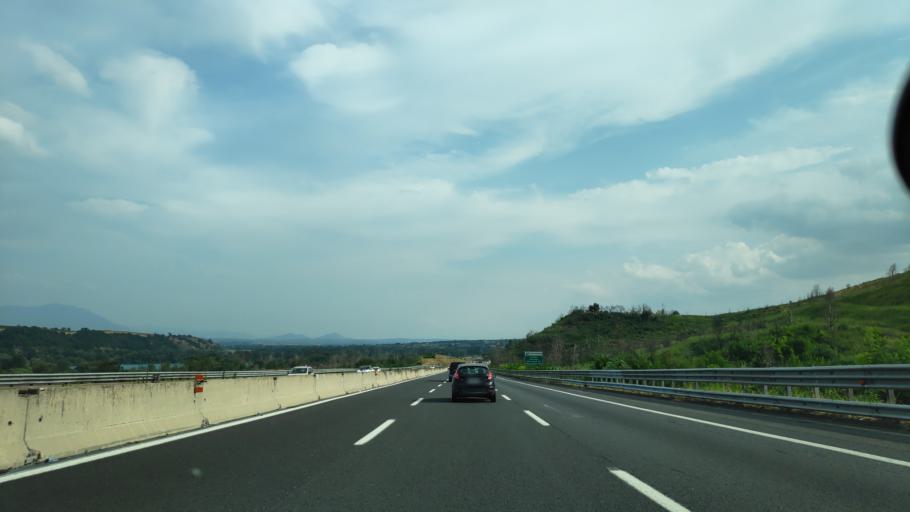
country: IT
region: Latium
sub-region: Citta metropolitana di Roma Capitale
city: Civitella San Paolo
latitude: 42.2003
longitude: 12.6026
